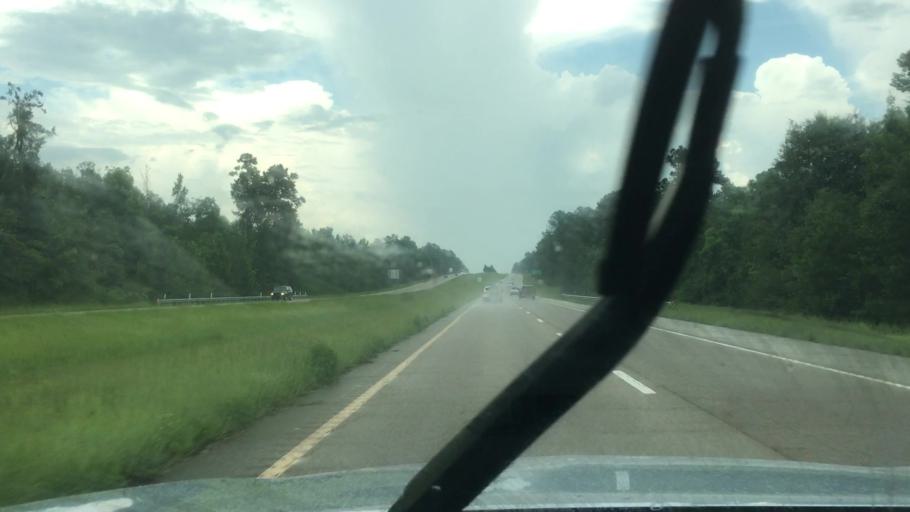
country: US
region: Mississippi
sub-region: Lamar County
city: Purvis
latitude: 31.1481
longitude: -89.3639
